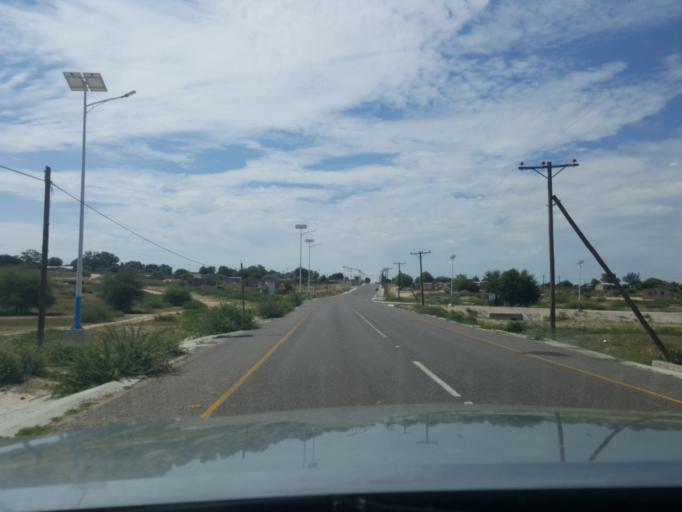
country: BW
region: Kweneng
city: Letlhakeng
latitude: -24.0911
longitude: 25.0302
